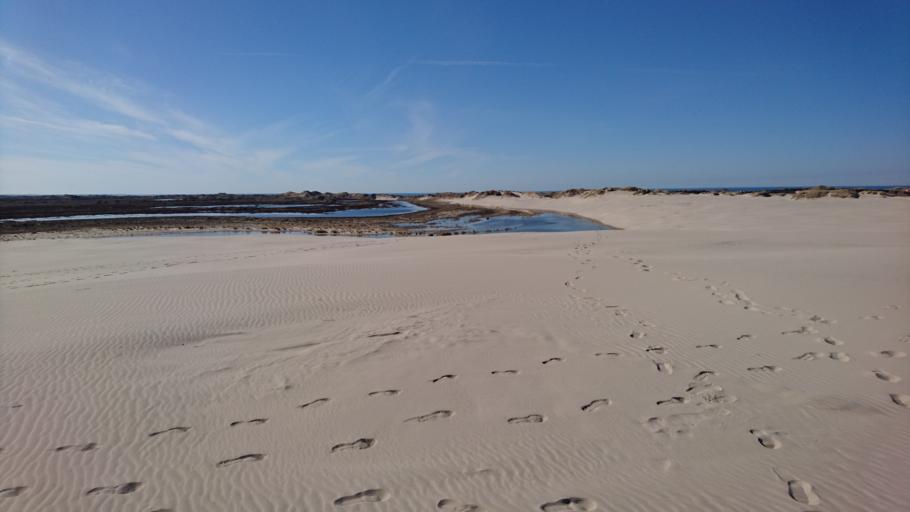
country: DK
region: North Denmark
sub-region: Frederikshavn Kommune
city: Strandby
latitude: 57.6485
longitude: 10.4081
